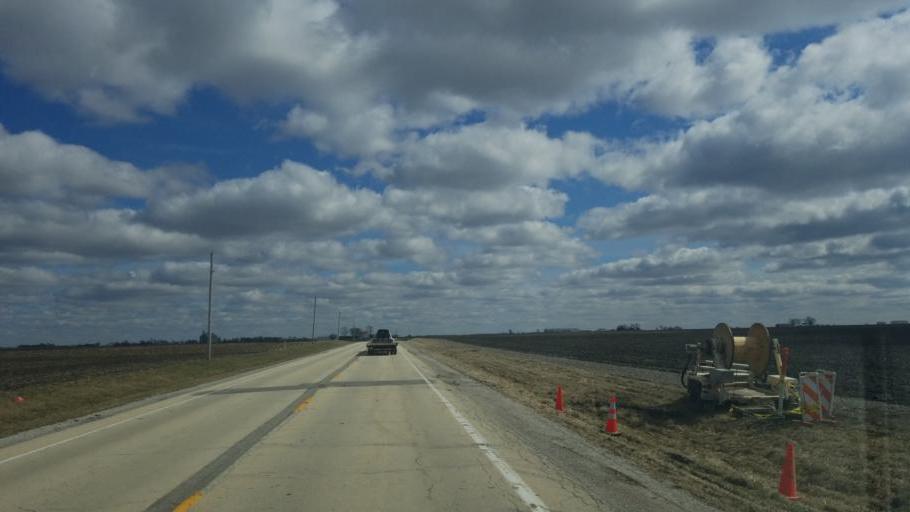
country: US
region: Illinois
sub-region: Moultrie County
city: Lovington
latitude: 39.7919
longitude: -88.5673
